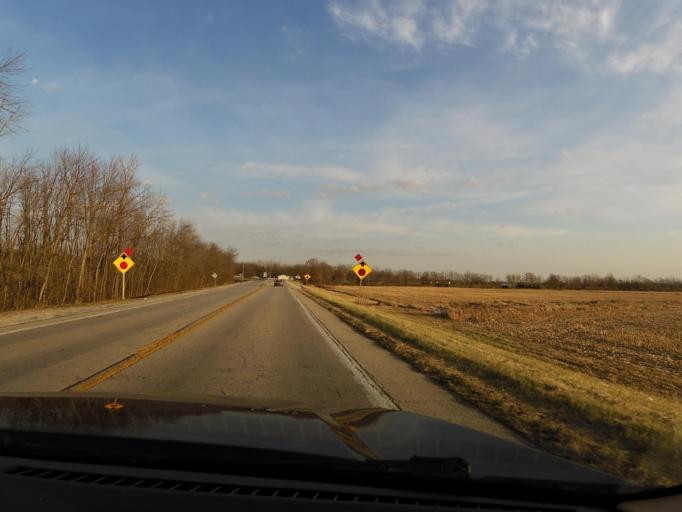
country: US
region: Illinois
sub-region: Fayette County
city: Vandalia
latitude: 38.9560
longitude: -89.0849
